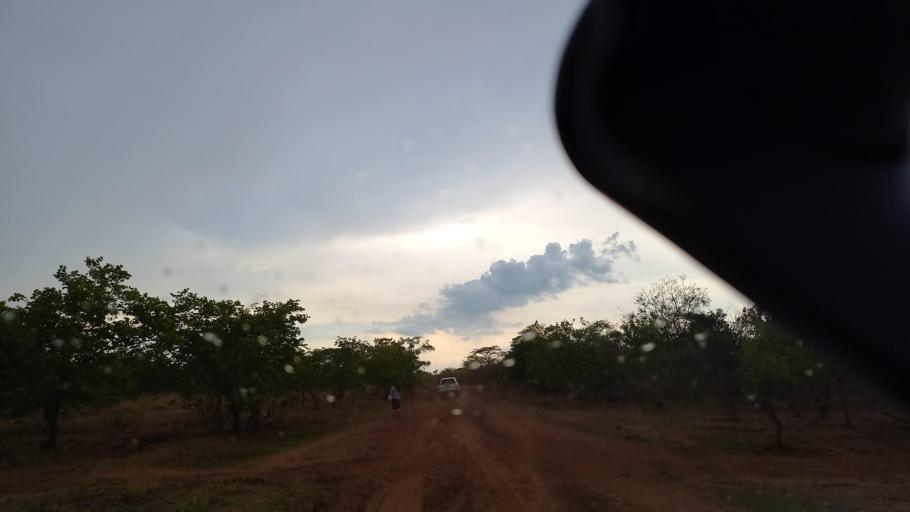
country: ZM
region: Lusaka
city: Kafue
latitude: -15.9826
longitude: 28.2610
